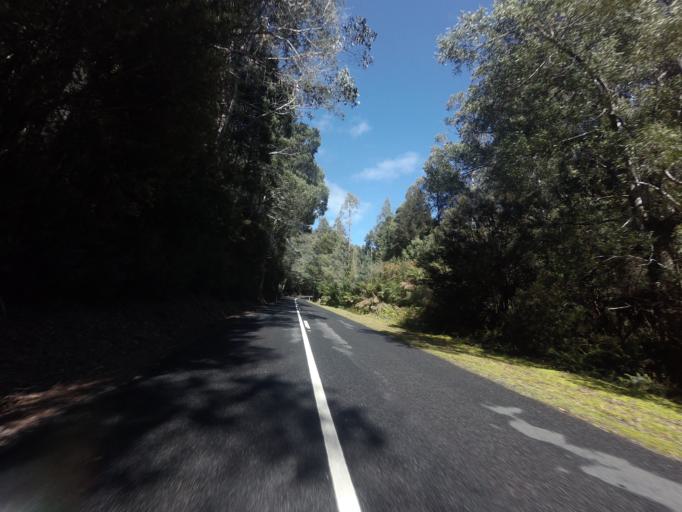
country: AU
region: Tasmania
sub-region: Derwent Valley
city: New Norfolk
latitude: -42.7522
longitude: 146.5156
